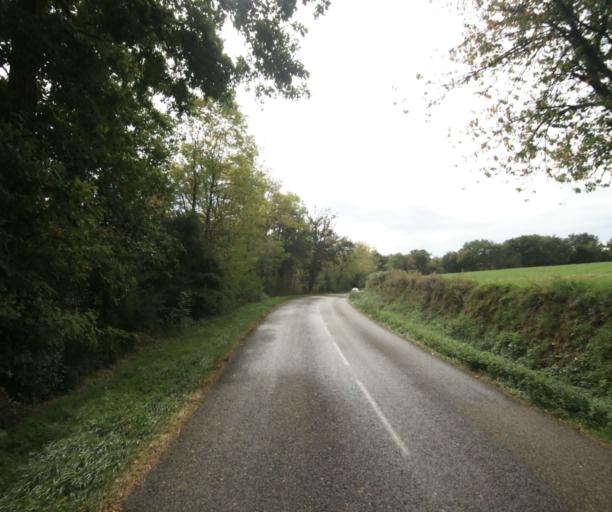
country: FR
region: Midi-Pyrenees
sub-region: Departement du Gers
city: Cazaubon
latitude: 43.8876
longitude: -0.0960
